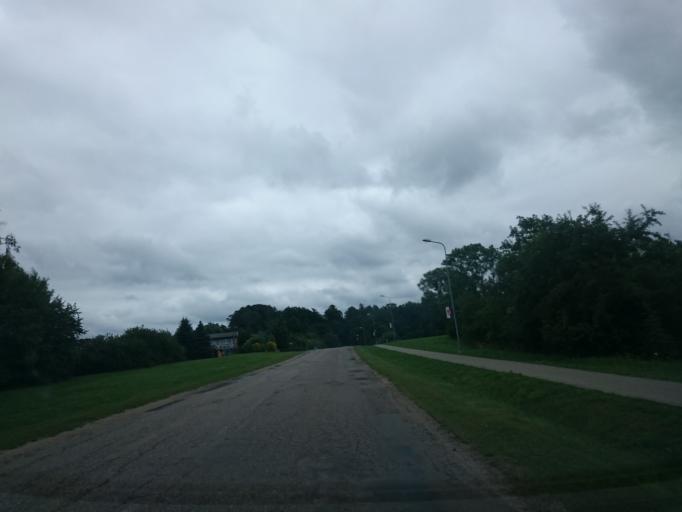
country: LV
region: Pavilostas
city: Pavilosta
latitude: 56.8821
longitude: 21.2068
